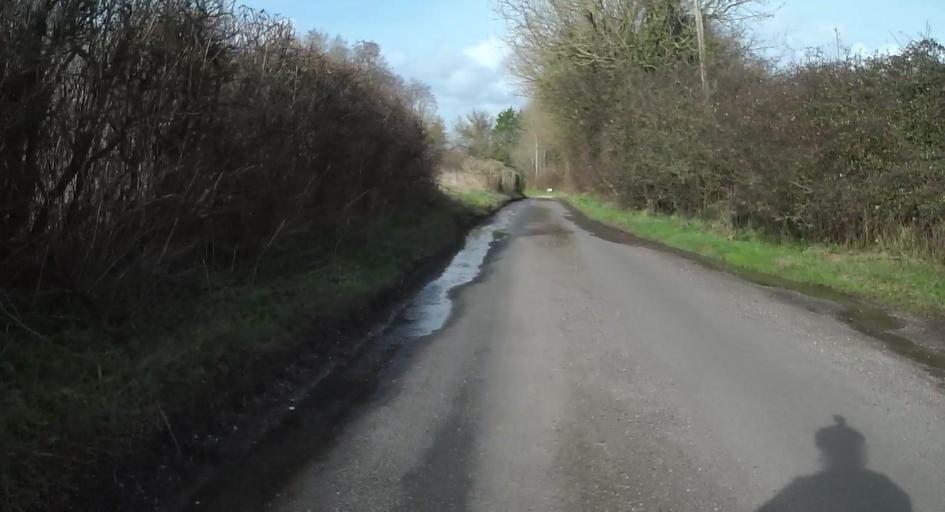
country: GB
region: England
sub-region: Hampshire
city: Kingsclere
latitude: 51.3451
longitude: -1.2406
